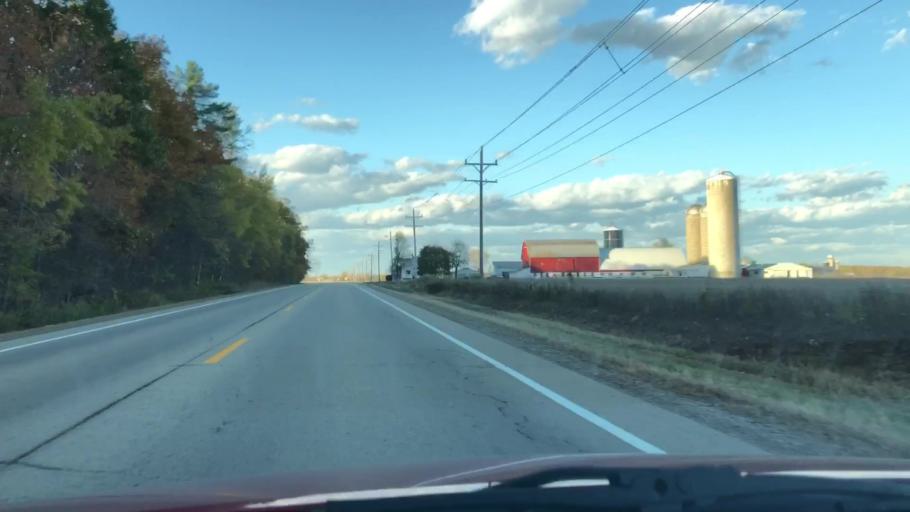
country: US
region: Wisconsin
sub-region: Outagamie County
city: Seymour
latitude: 44.4914
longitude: -88.2913
